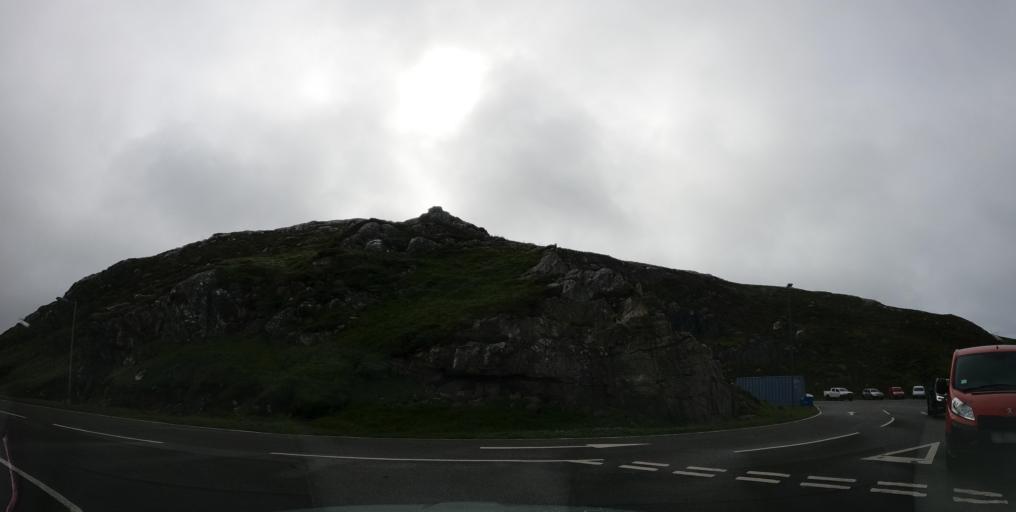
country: GB
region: Scotland
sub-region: Eilean Siar
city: Barra
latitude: 57.0706
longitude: -7.3077
